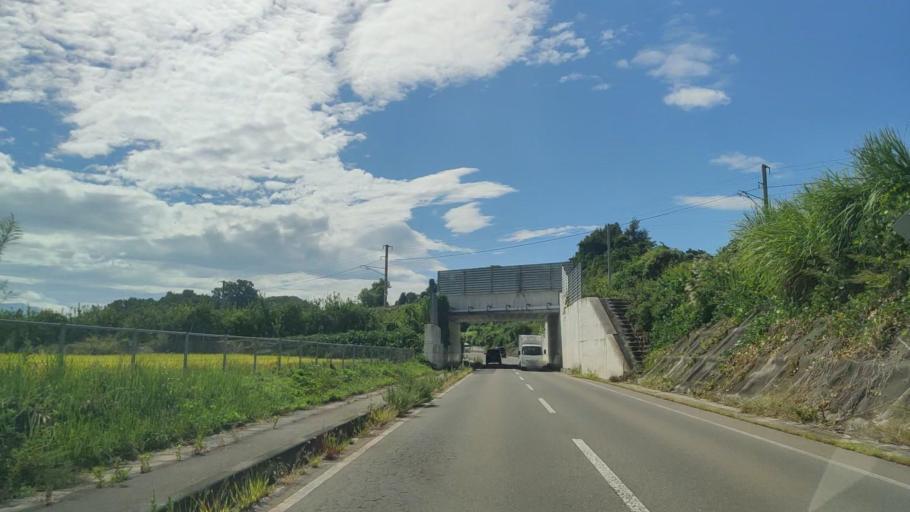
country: JP
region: Nagano
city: Nakano
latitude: 36.7266
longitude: 138.2898
